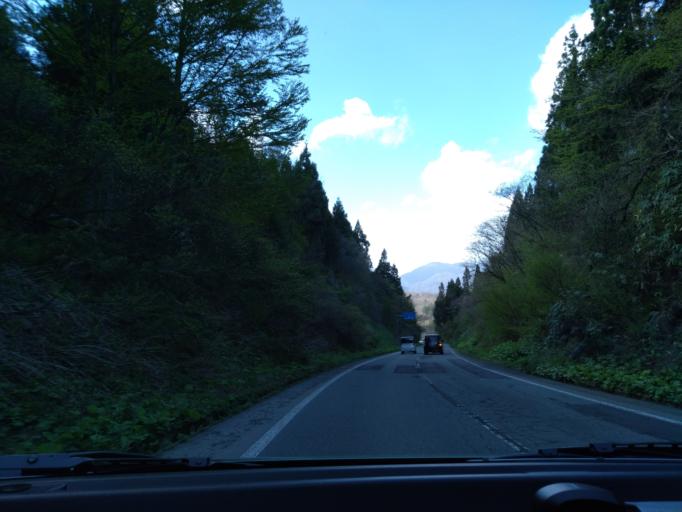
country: JP
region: Akita
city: Akita
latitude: 39.6904
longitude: 140.2748
